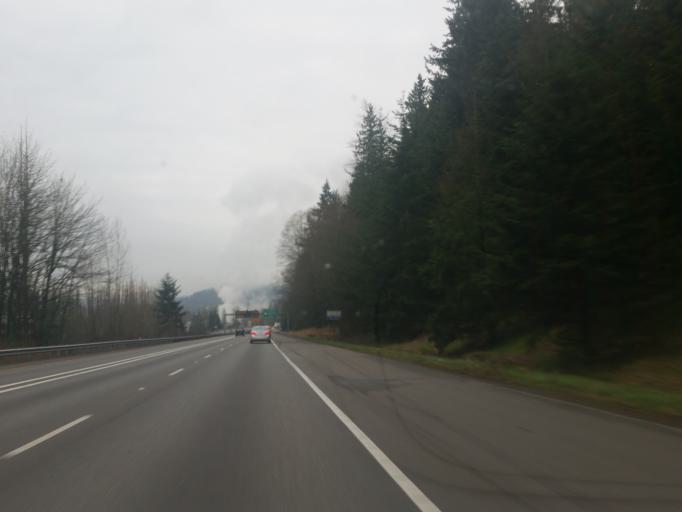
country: US
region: Washington
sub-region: King County
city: Bothell
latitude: 47.7806
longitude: -122.1942
